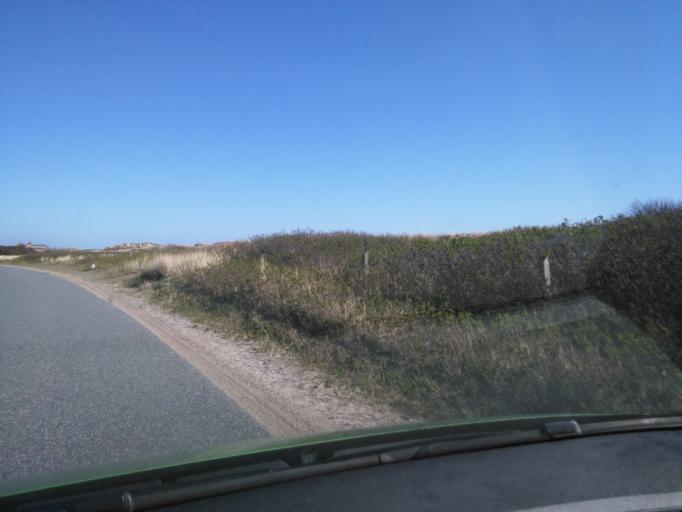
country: DK
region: South Denmark
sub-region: Varde Kommune
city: Oksbol
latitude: 55.5533
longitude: 8.0960
